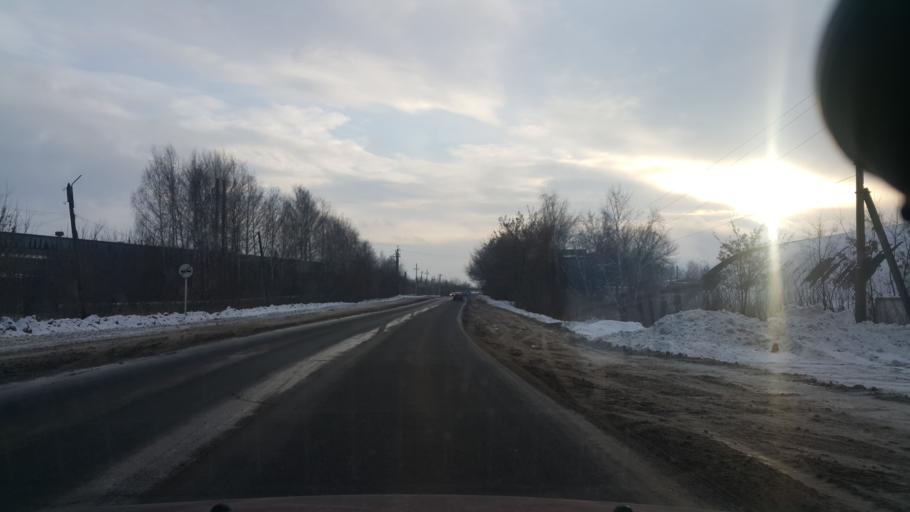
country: RU
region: Tambov
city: Pokrovo-Prigorodnoye
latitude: 52.6582
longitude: 41.4234
